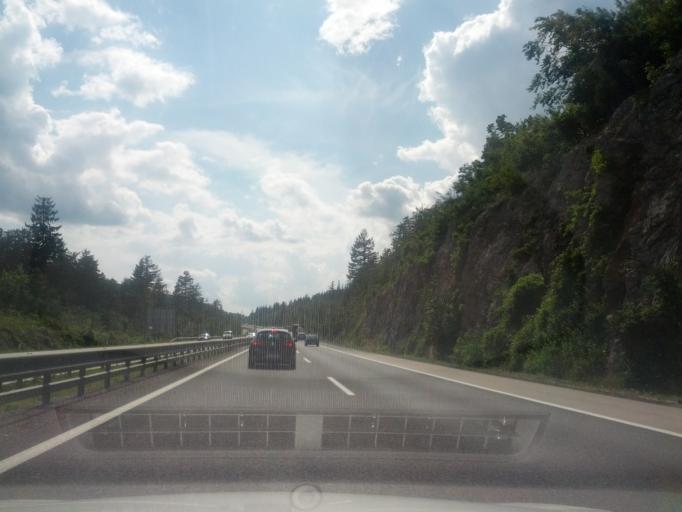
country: SI
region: Cerknica
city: Rakek
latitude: 45.8056
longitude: 14.2757
